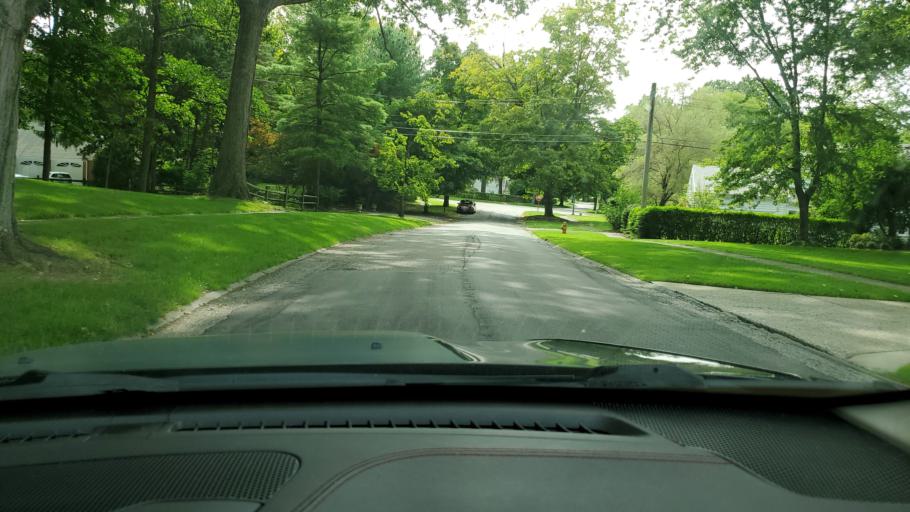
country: US
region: Ohio
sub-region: Mahoning County
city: Boardman
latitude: 41.0535
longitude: -80.6666
